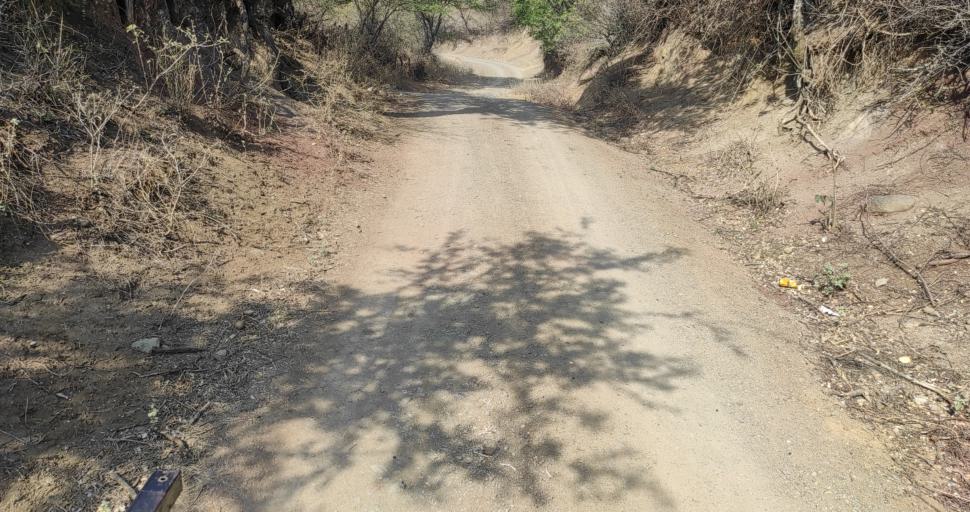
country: EC
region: Loja
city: Catacocha
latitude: -4.0086
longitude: -79.6987
